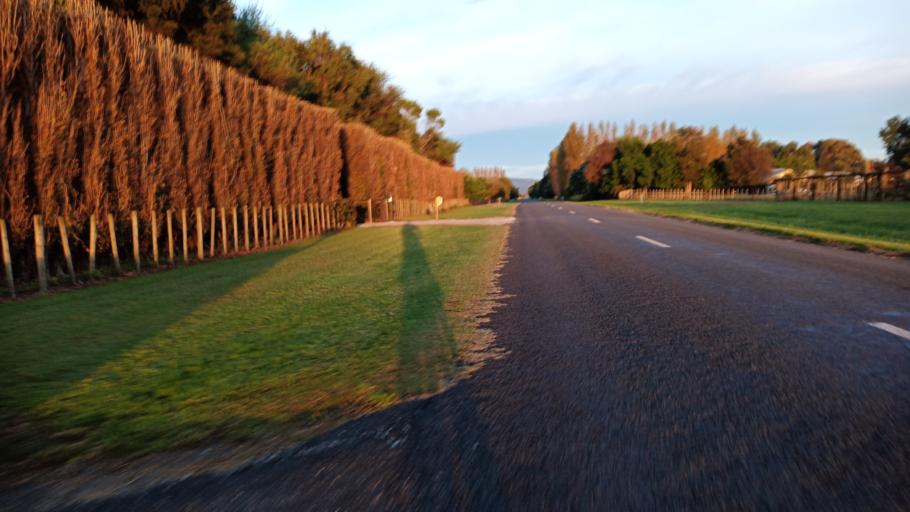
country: NZ
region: Gisborne
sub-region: Gisborne District
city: Gisborne
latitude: -38.6337
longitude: 177.9824
